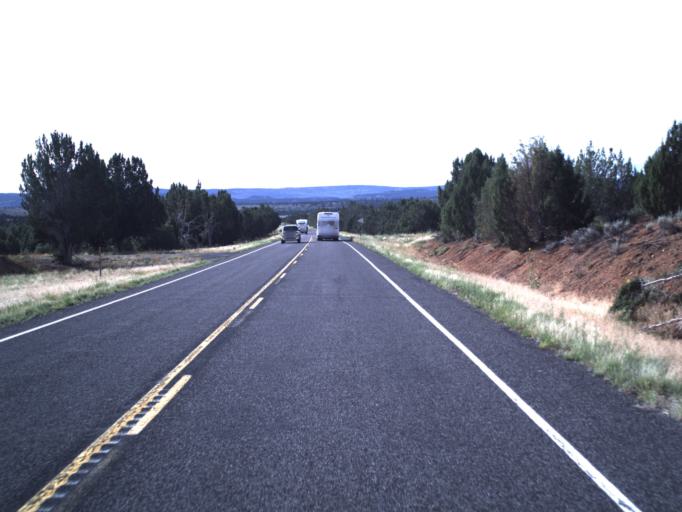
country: US
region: Utah
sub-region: Kane County
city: Kanab
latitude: 37.2514
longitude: -112.7612
